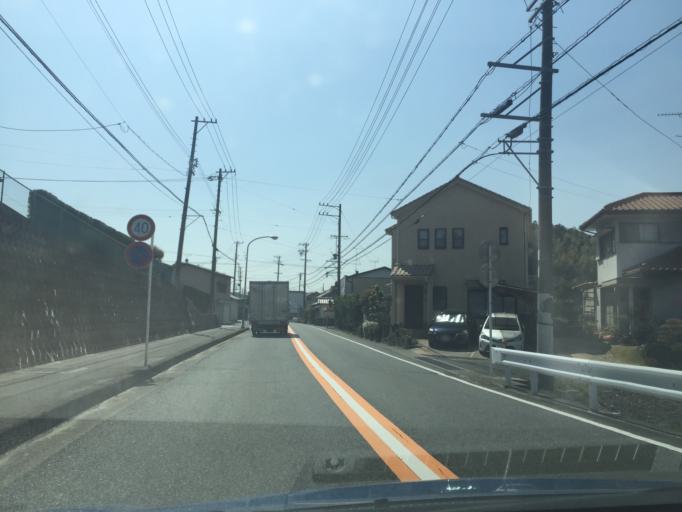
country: JP
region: Shizuoka
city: Hamamatsu
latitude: 34.7893
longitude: 137.6467
